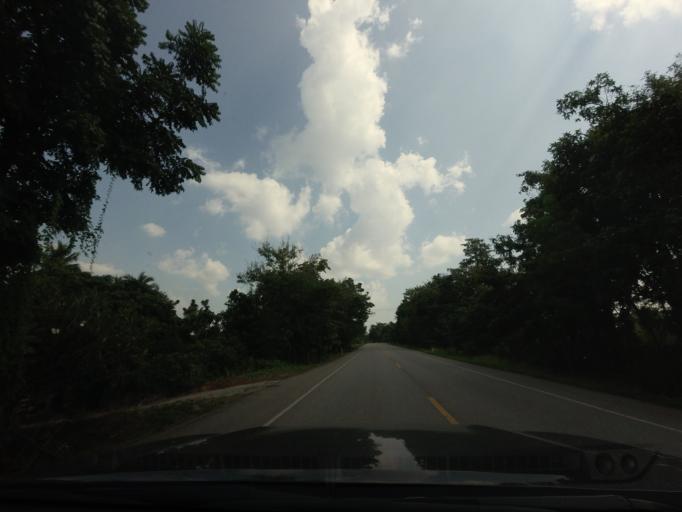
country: TH
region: Phitsanulok
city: Chat Trakan
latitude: 17.2696
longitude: 100.5463
